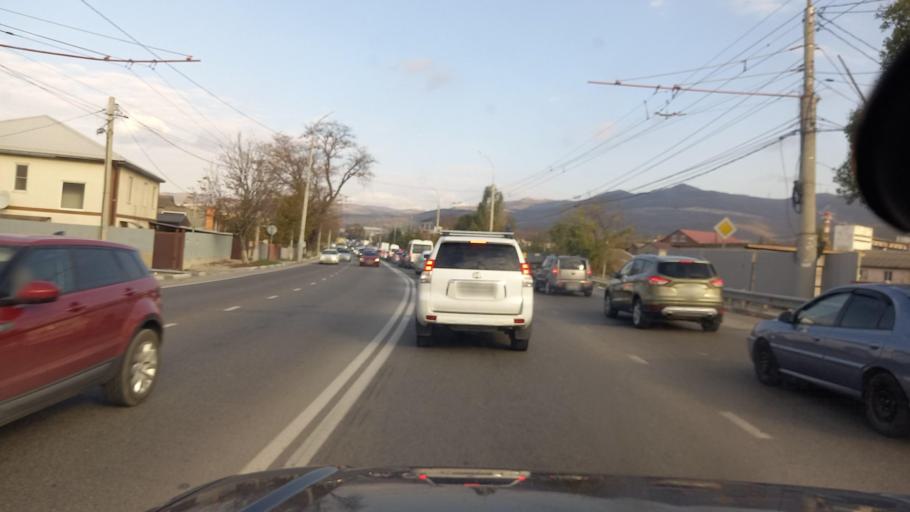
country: RU
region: Krasnodarskiy
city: Gayduk
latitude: 44.7513
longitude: 37.7275
